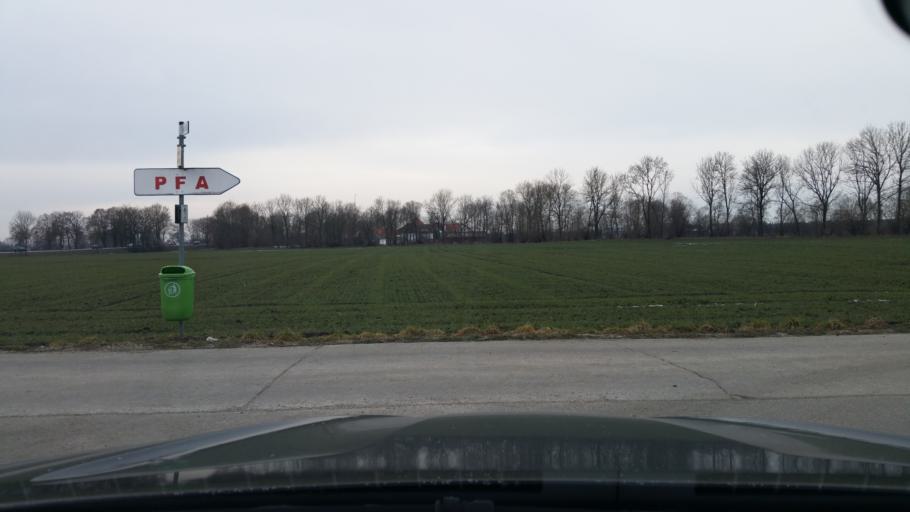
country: DE
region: Bavaria
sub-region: Lower Bavaria
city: Bruckberg
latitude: 48.4855
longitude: 12.0119
